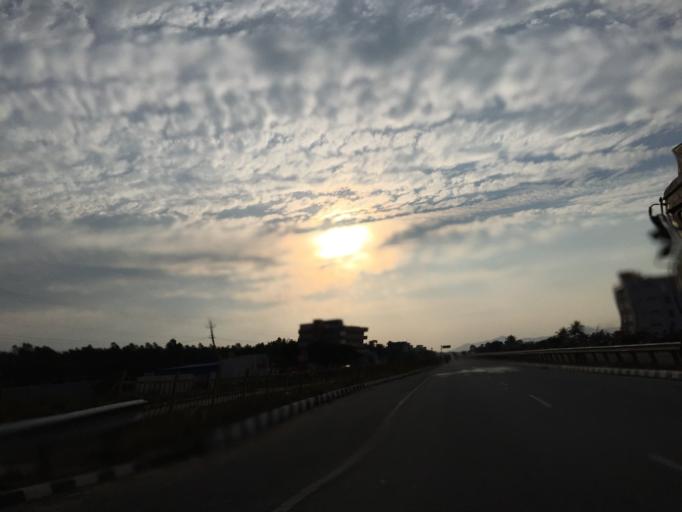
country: IN
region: Karnataka
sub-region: Kolar
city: Kolar
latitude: 13.1328
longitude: 78.1695
